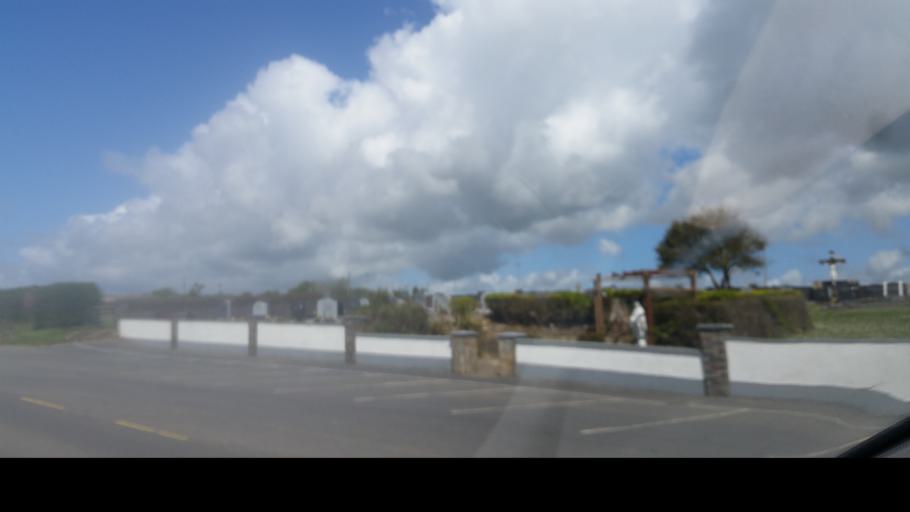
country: IE
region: Munster
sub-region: Waterford
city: Dunmore East
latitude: 52.2236
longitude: -6.9322
